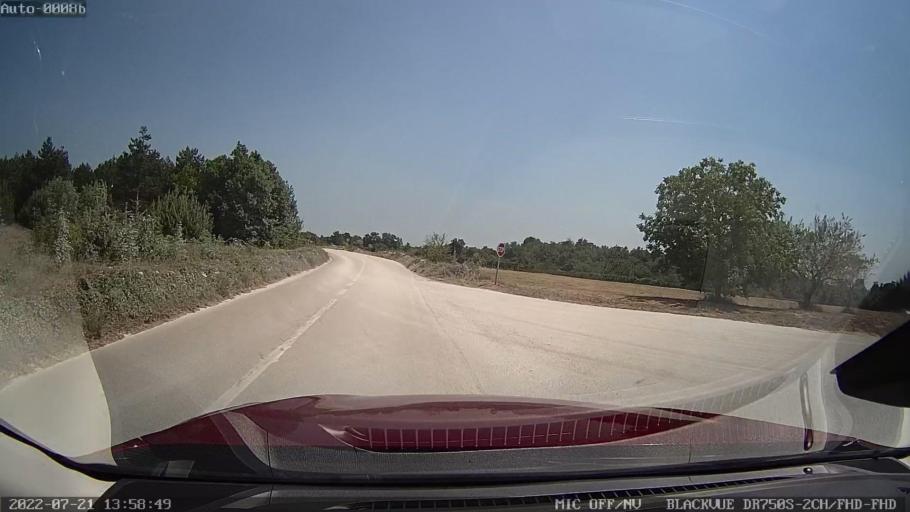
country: HR
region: Istarska
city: Vodnjan
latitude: 45.1069
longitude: 13.8568
